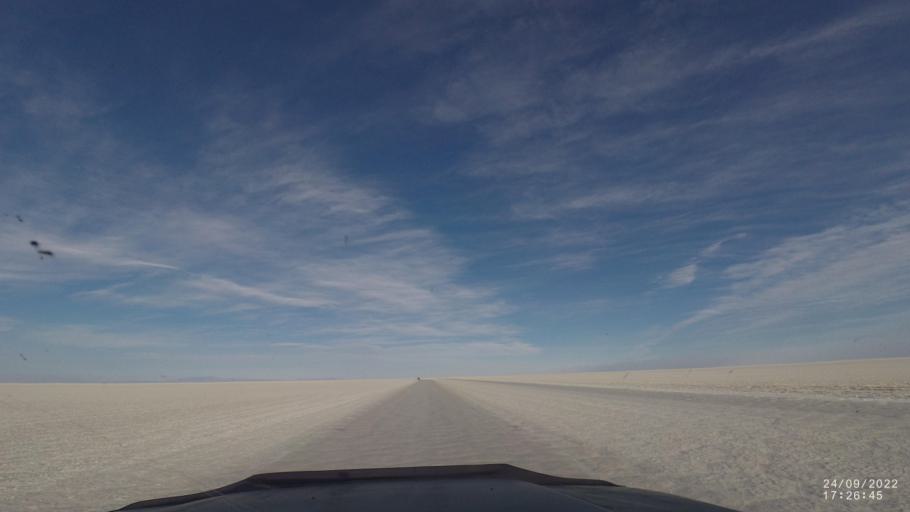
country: BO
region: Potosi
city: Colchani
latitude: -20.2969
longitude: -67.4627
